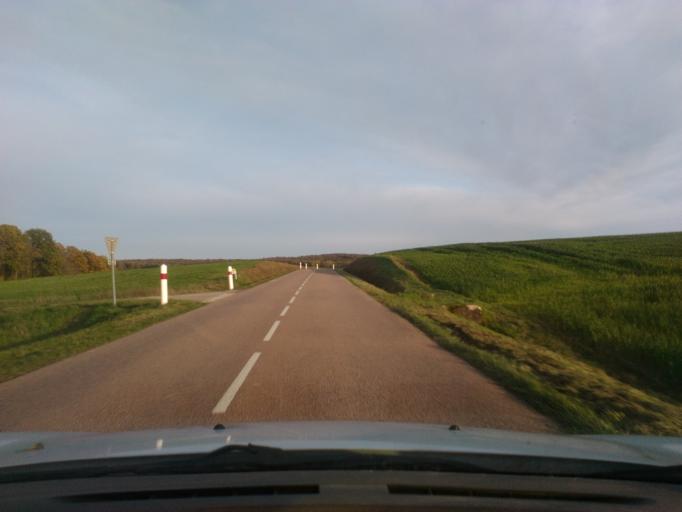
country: FR
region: Lorraine
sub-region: Departement des Vosges
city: Mirecourt
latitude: 48.2233
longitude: 6.1525
